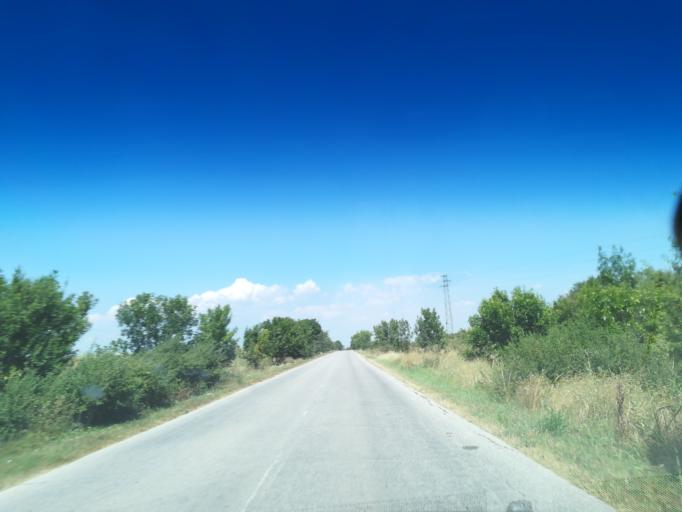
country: BG
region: Plovdiv
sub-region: Obshtina Sadovo
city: Sadovo
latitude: 42.0503
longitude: 25.1458
